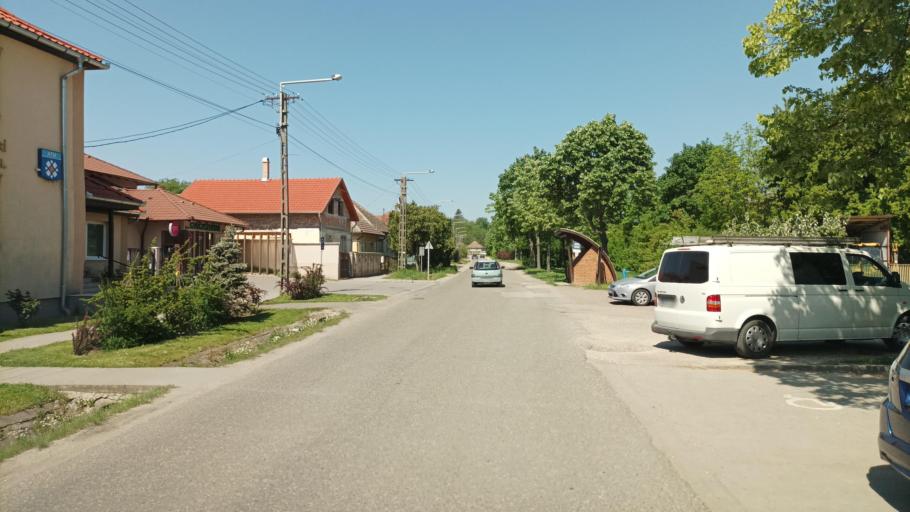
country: HU
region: Pest
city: Uri
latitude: 47.4142
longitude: 19.5240
